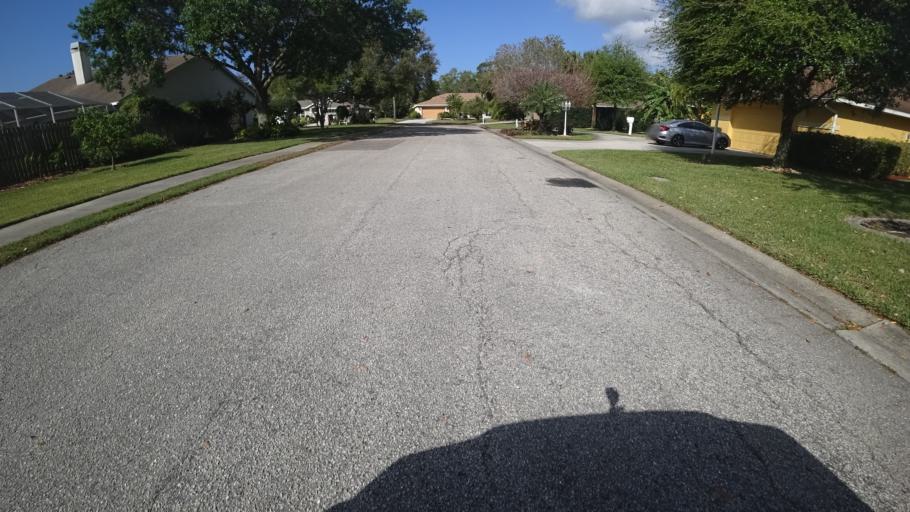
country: US
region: Florida
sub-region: Manatee County
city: Whitfield
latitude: 27.4253
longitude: -82.5620
